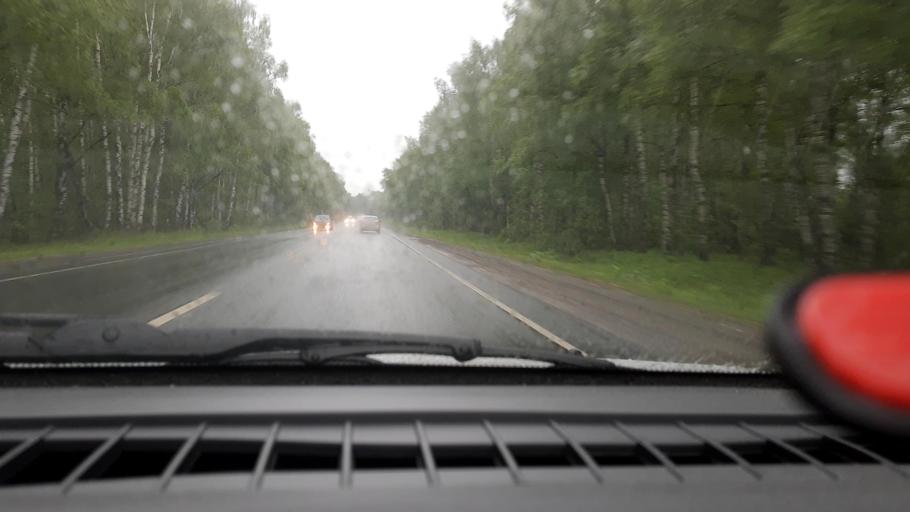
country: RU
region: Nizjnij Novgorod
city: Linda
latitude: 56.5528
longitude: 44.0222
